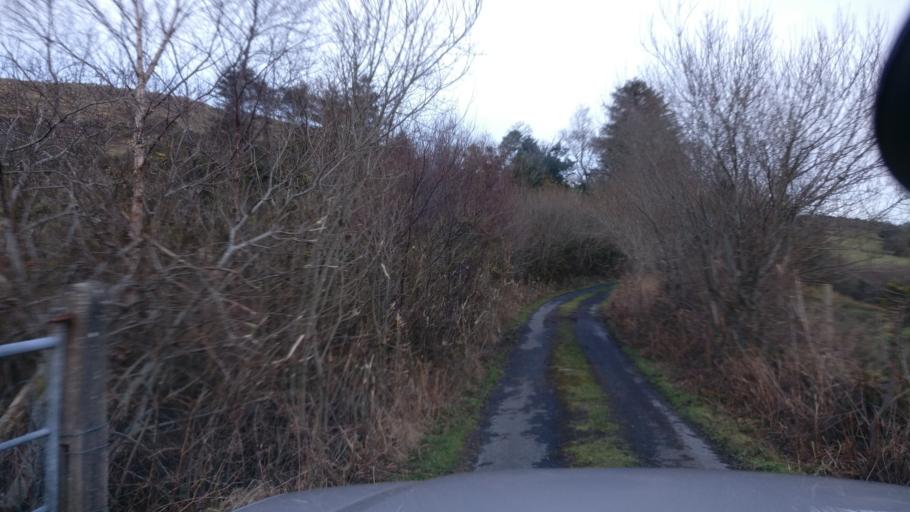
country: IE
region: Connaught
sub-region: County Galway
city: Oughterard
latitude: 53.5207
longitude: -9.4238
